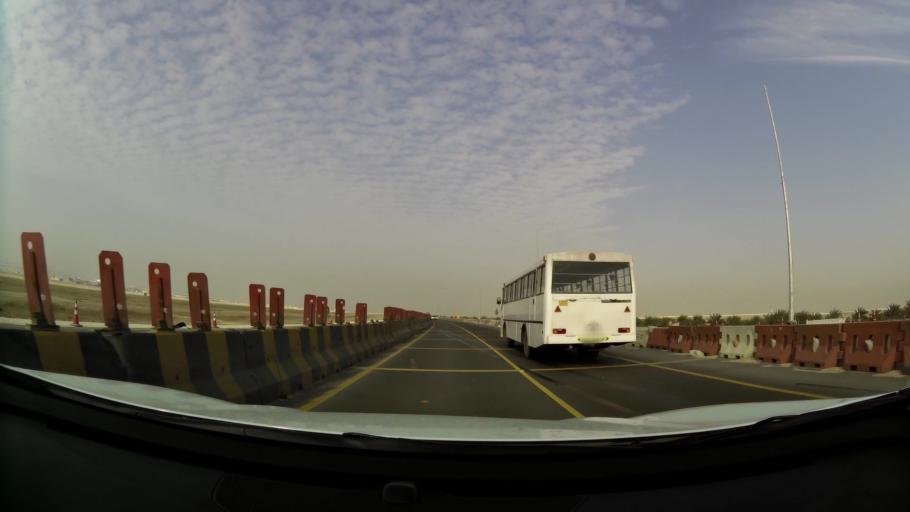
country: AE
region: Abu Dhabi
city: Abu Dhabi
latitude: 24.2561
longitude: 54.4832
